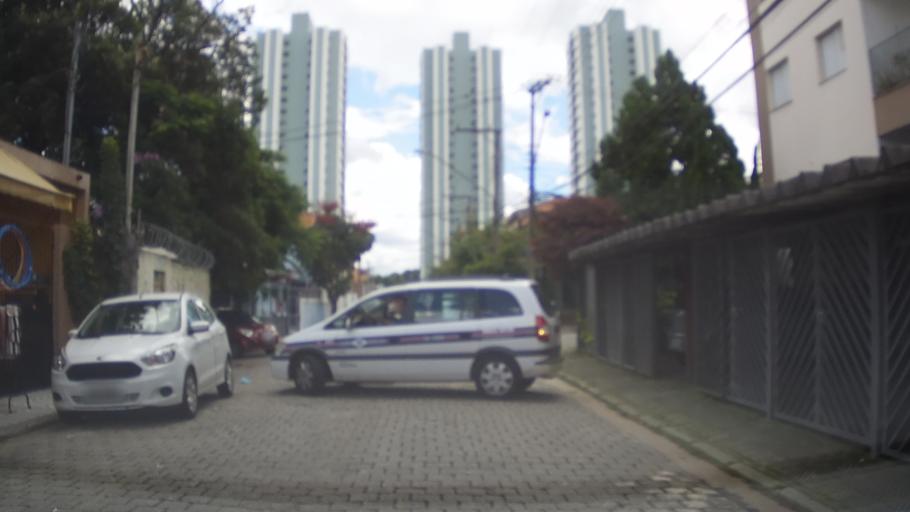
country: BR
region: Sao Paulo
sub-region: Guarulhos
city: Guarulhos
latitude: -23.4624
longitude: -46.5466
